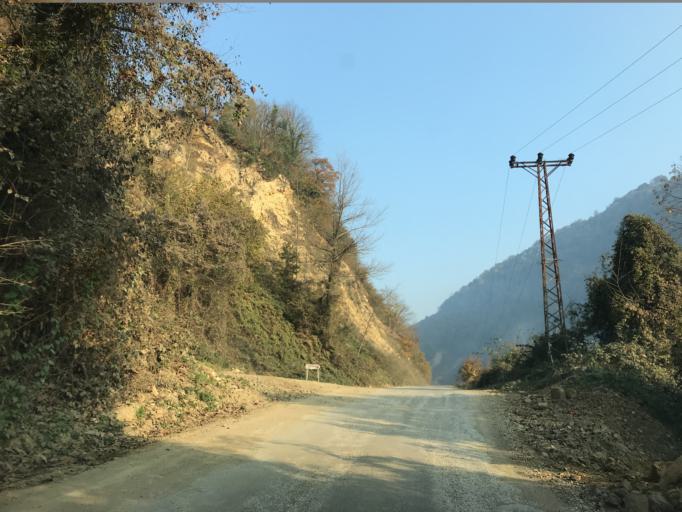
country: TR
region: Duzce
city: Cumayeri
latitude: 40.9219
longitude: 30.9287
